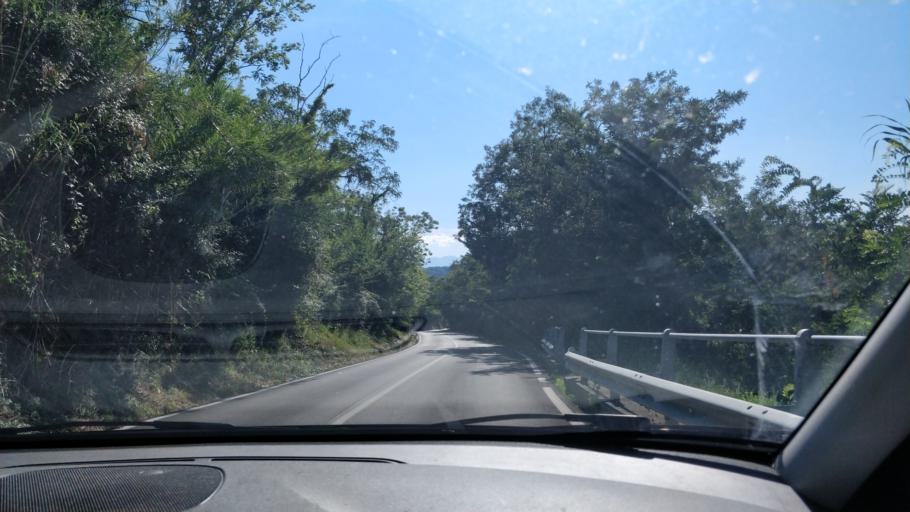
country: IT
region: Abruzzo
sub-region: Provincia di Pescara
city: Serramonacesca
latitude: 42.2549
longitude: 14.0880
